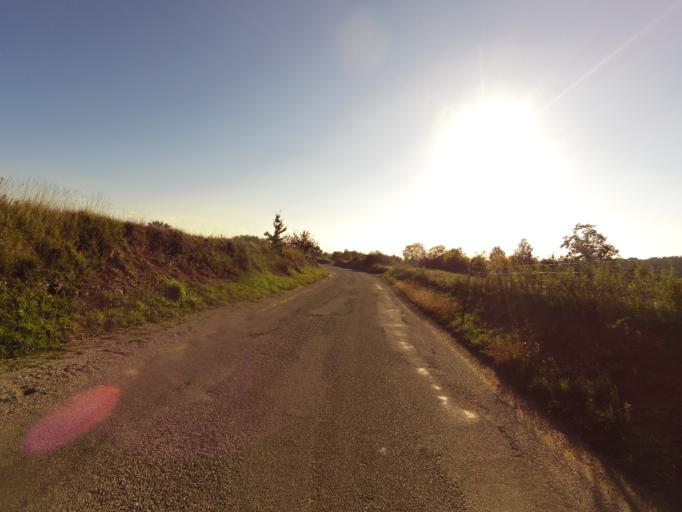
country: FR
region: Rhone-Alpes
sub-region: Departement de l'Ardeche
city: Largentiere
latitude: 44.5199
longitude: 4.2974
